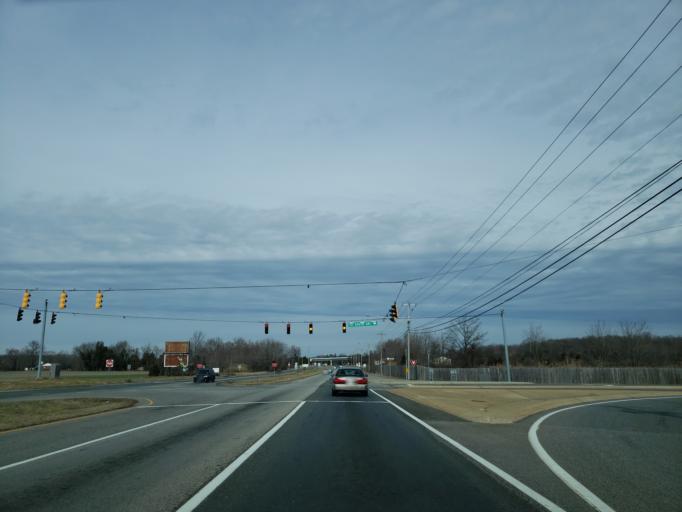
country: US
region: Delaware
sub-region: Kent County
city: Smyrna
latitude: 39.3245
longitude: -75.6214
